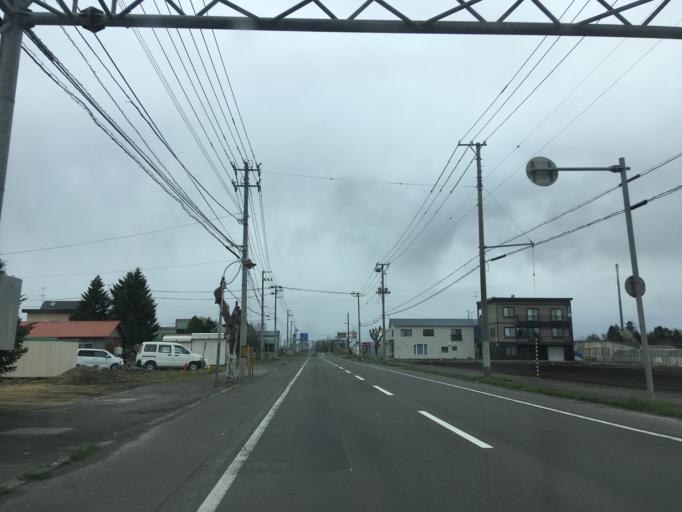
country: JP
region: Hokkaido
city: Chitose
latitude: 42.9473
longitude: 141.8032
